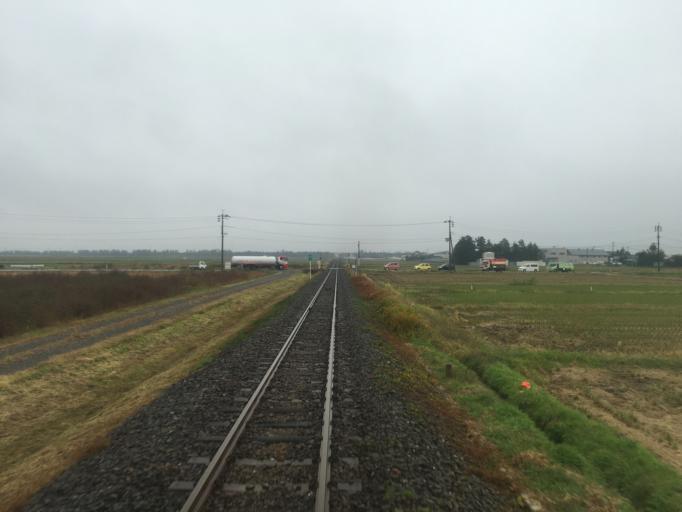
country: JP
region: Miyagi
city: Furukawa
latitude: 38.5739
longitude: 140.9143
